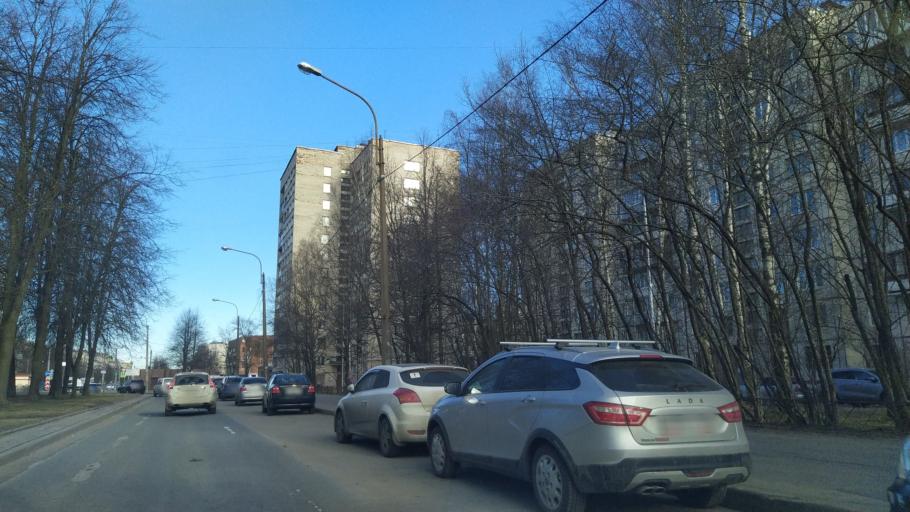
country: RU
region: Leningrad
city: Akademicheskoe
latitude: 60.0052
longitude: 30.4217
